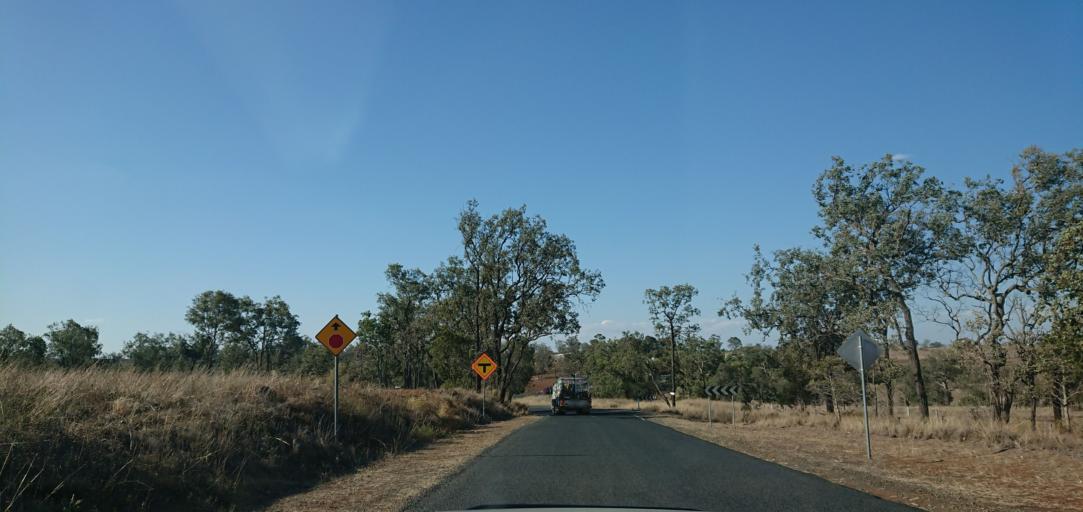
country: AU
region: Queensland
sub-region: Toowoomba
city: Westbrook
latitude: -27.6488
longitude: 151.7267
